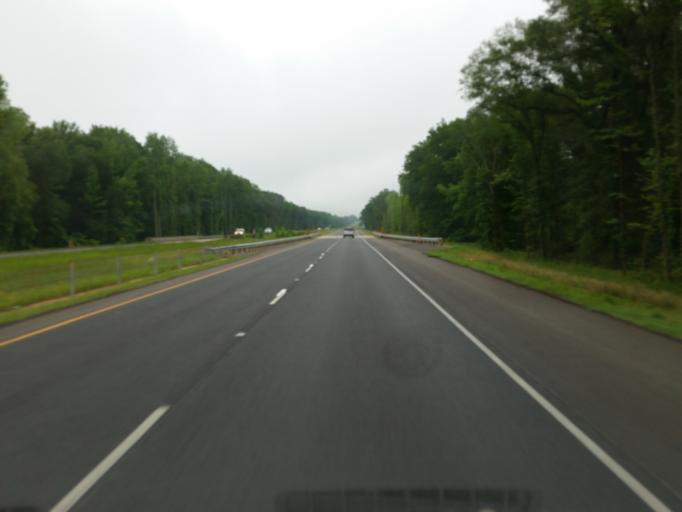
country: US
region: Louisiana
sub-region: Bienville Parish
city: Arcadia
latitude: 32.5630
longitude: -93.0991
